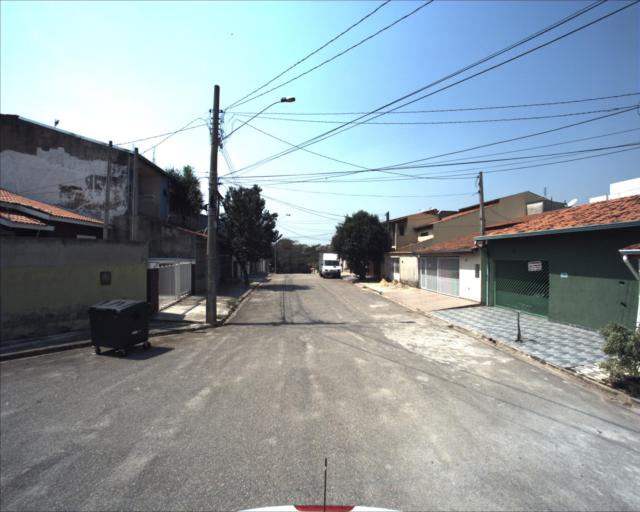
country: BR
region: Sao Paulo
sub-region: Sorocaba
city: Sorocaba
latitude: -23.4397
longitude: -47.4856
